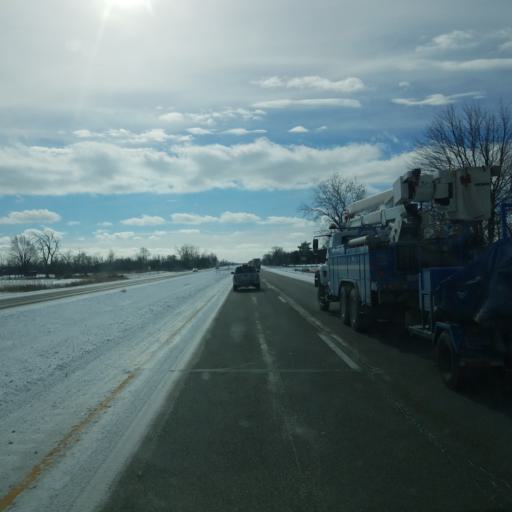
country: US
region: Michigan
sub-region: Gratiot County
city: Ithaca
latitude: 43.2065
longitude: -84.5634
